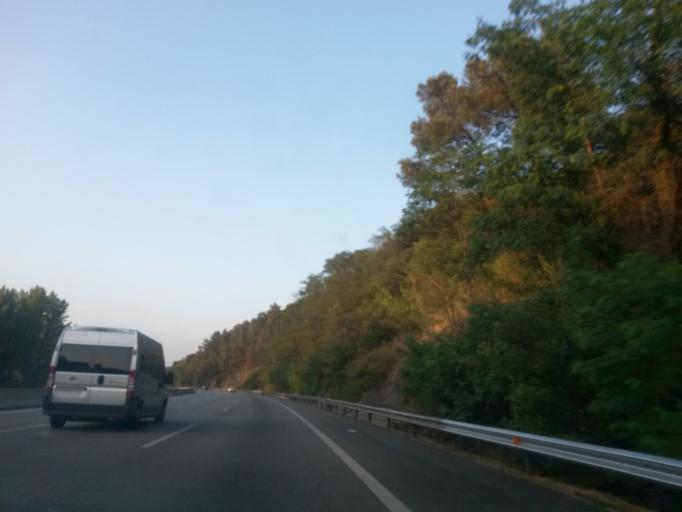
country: ES
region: Catalonia
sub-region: Provincia de Barcelona
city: Sant Celoni
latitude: 41.6927
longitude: 2.5101
